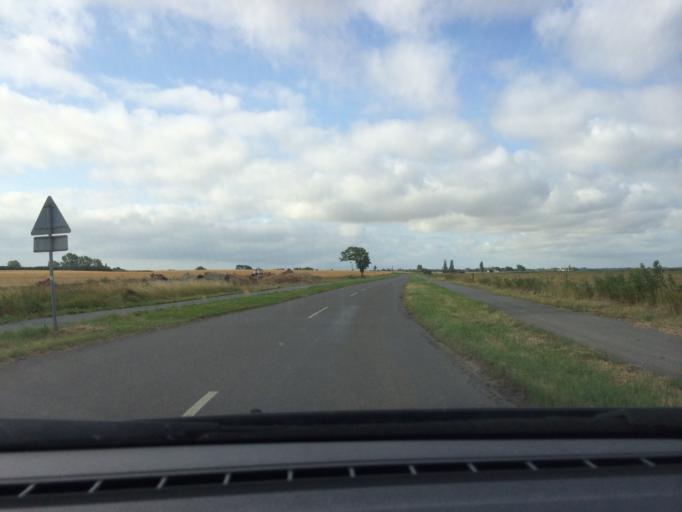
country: DK
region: Zealand
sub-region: Vordingborg Kommune
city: Stege
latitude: 55.0193
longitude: 12.2901
